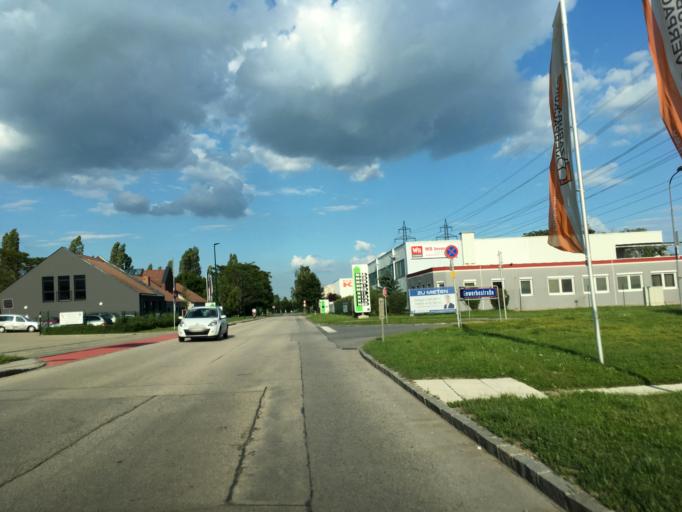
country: AT
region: Lower Austria
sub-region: Politischer Bezirk Modling
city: Wiener Neudorf
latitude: 48.0799
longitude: 16.3211
